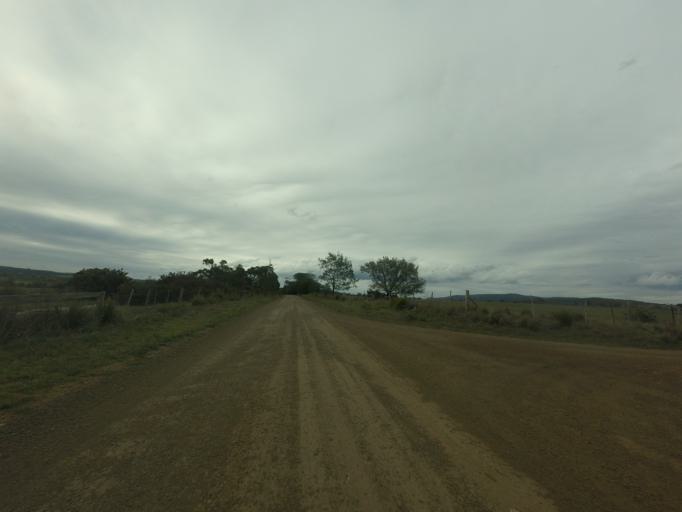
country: AU
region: Tasmania
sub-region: Break O'Day
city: St Helens
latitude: -41.9910
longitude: 148.0668
